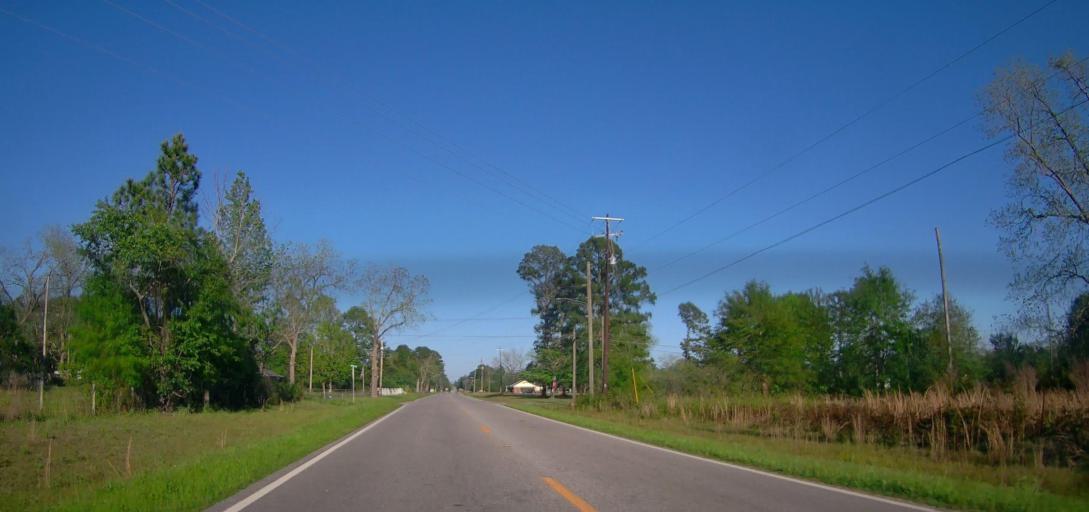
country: US
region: Georgia
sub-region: Ben Hill County
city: Fitzgerald
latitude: 31.7437
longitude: -83.2530
